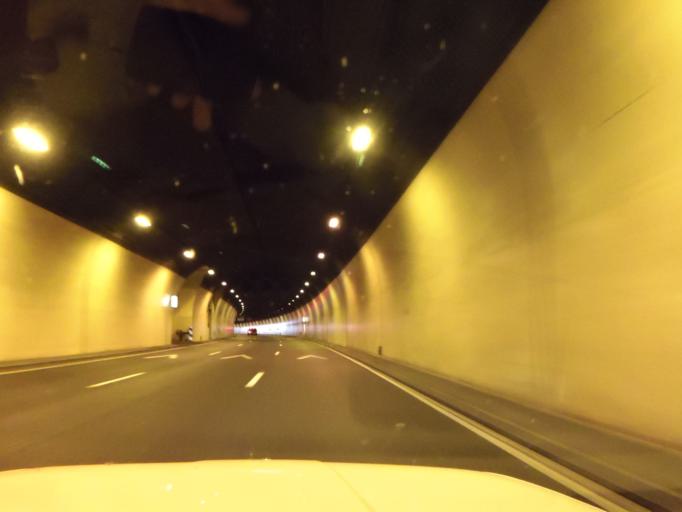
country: FR
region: Rhone-Alpes
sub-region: Departement du Rhone
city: Ecully
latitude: 45.7776
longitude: 4.7926
